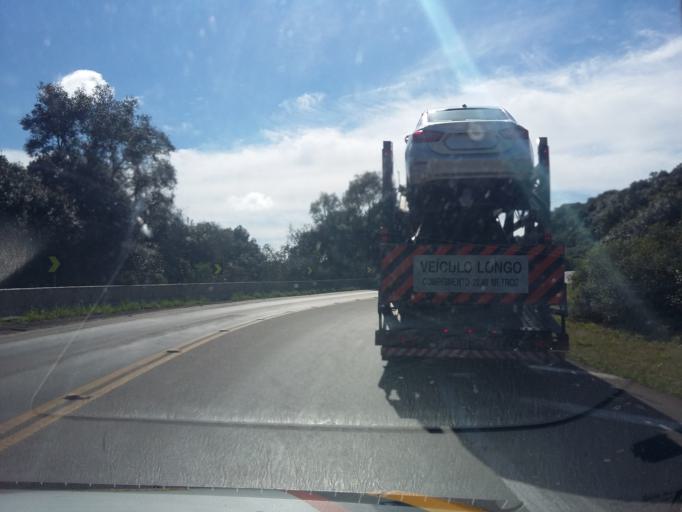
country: BR
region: Rio Grande do Sul
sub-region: Vacaria
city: Vacaria
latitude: -28.5853
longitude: -51.0289
